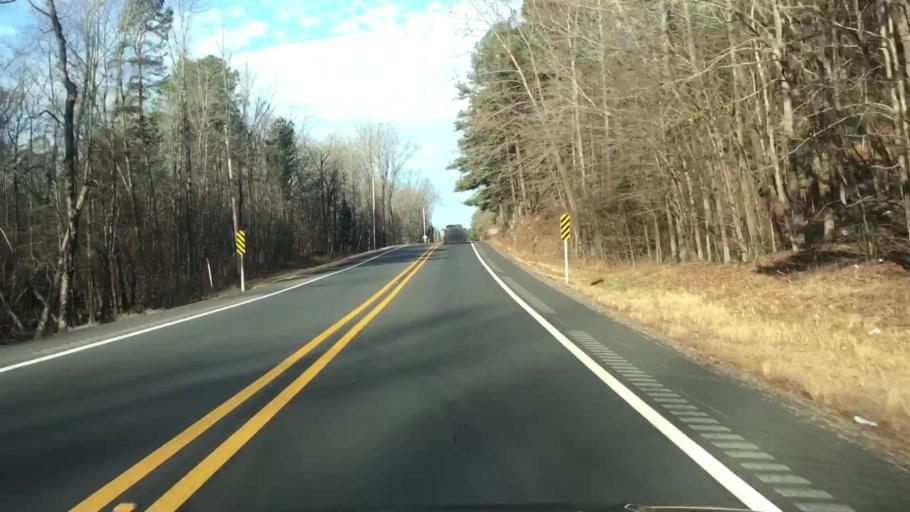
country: US
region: Arkansas
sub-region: Montgomery County
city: Mount Ida
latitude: 34.5237
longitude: -93.4122
